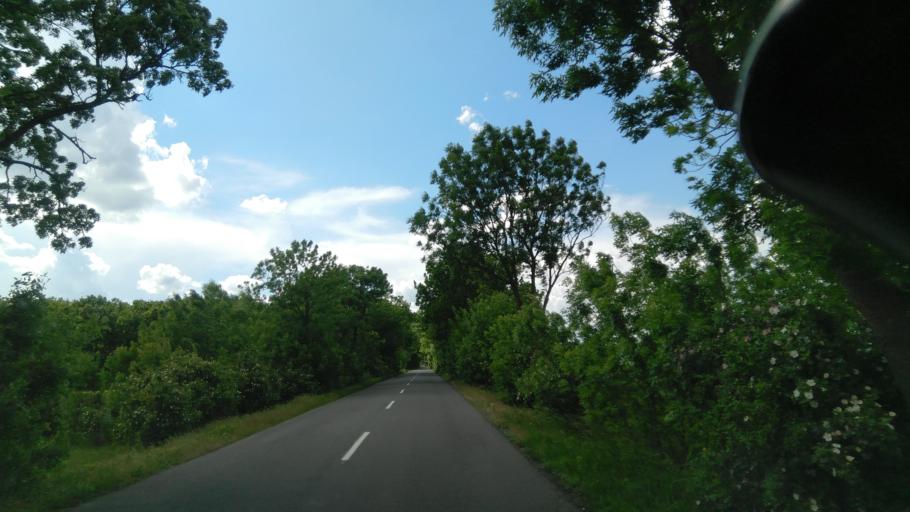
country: HU
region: Bekes
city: Bucsa
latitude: 47.1808
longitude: 21.0495
